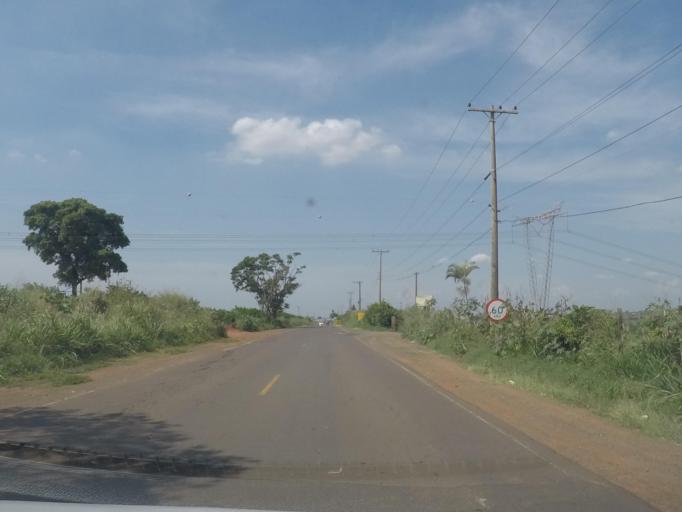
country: BR
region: Sao Paulo
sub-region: Sumare
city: Sumare
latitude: -22.8653
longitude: -47.2952
